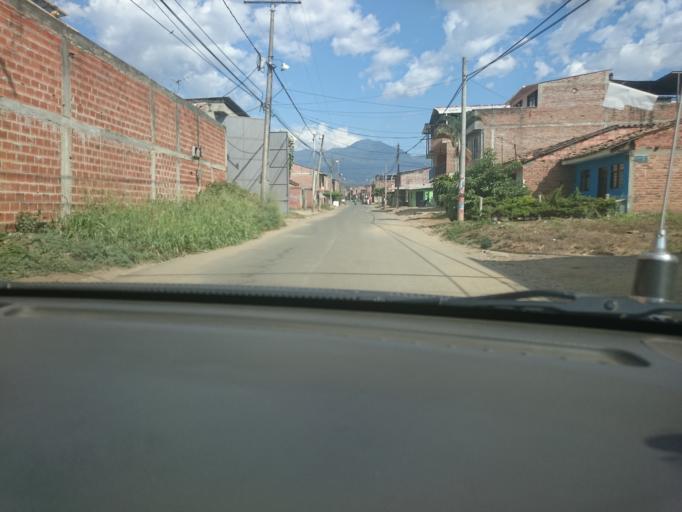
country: CO
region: Cauca
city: Santander de Quilichao
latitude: 3.0150
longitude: -76.4915
